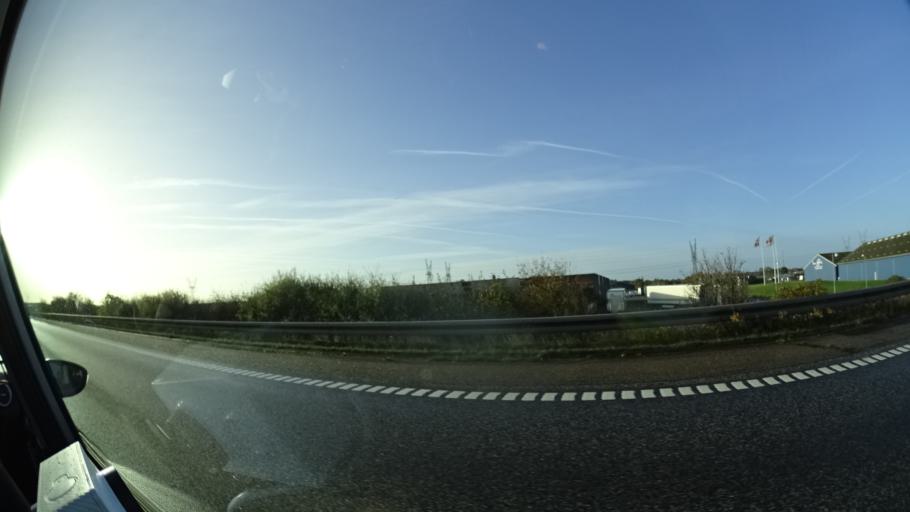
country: DK
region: South Denmark
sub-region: Fredericia Kommune
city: Taulov
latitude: 55.5443
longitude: 9.6468
